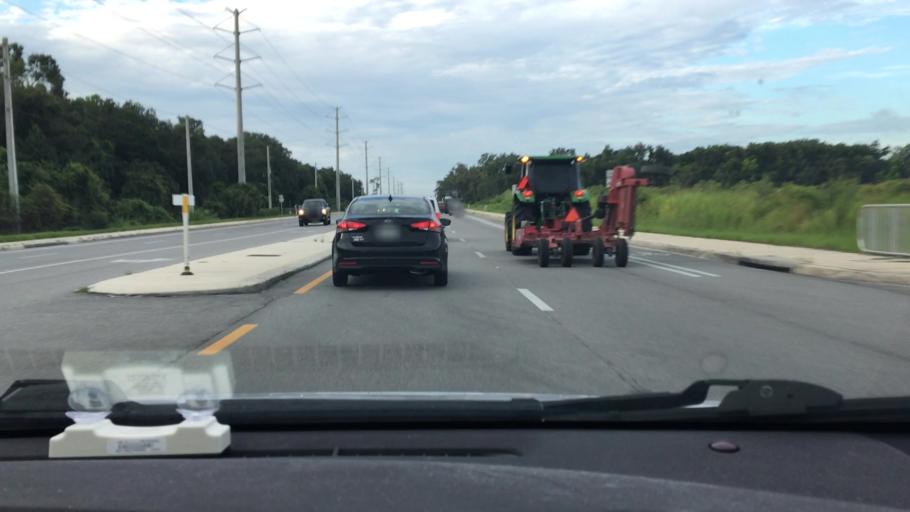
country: US
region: Florida
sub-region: Seminole County
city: Midway
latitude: 28.7966
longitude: -81.2122
